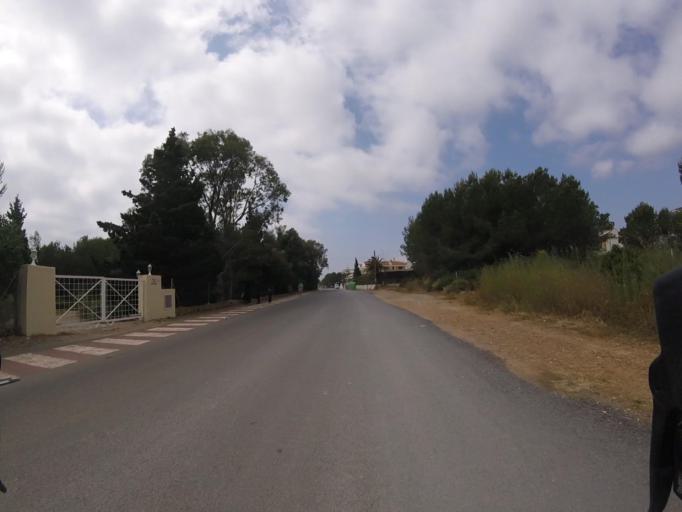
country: ES
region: Valencia
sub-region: Provincia de Castello
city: Alcoceber
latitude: 40.2577
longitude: 0.2942
